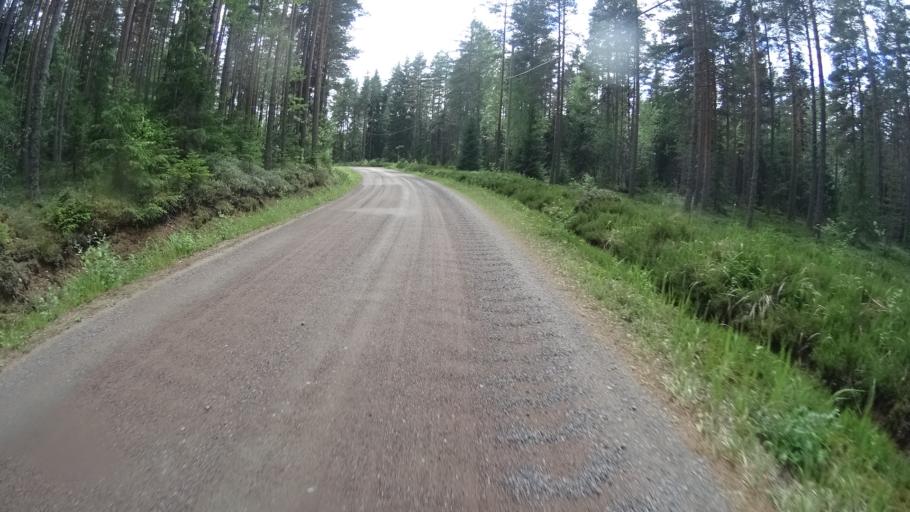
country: FI
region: Uusimaa
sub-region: Helsinki
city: Karkkila
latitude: 60.6032
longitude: 24.1816
